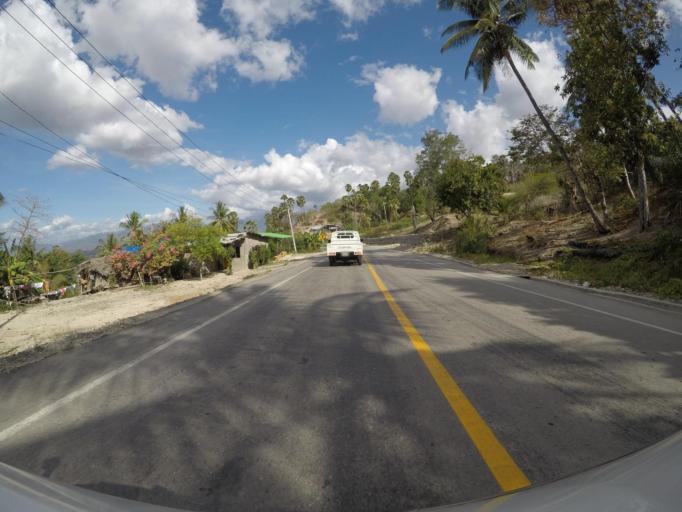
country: TL
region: Baucau
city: Baucau
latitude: -8.4645
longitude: 126.4822
